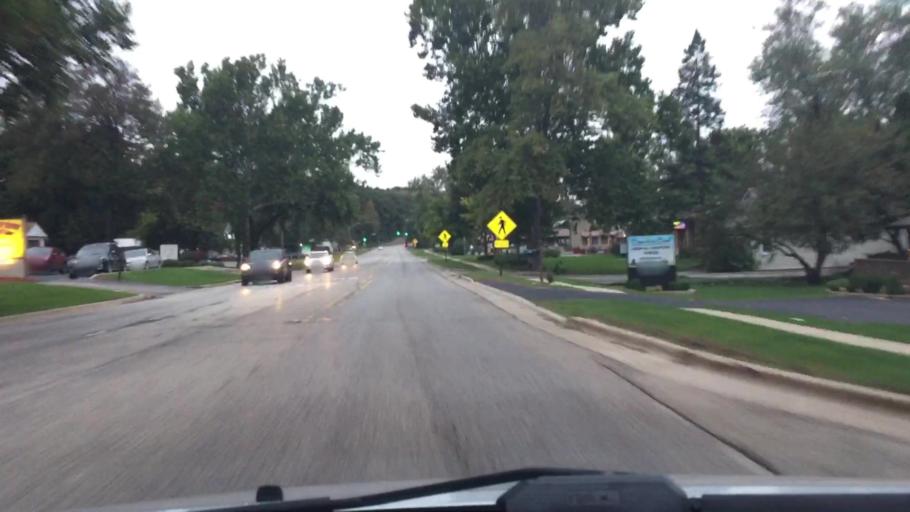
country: US
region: Illinois
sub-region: McHenry County
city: Algonquin
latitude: 42.1547
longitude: -88.2958
